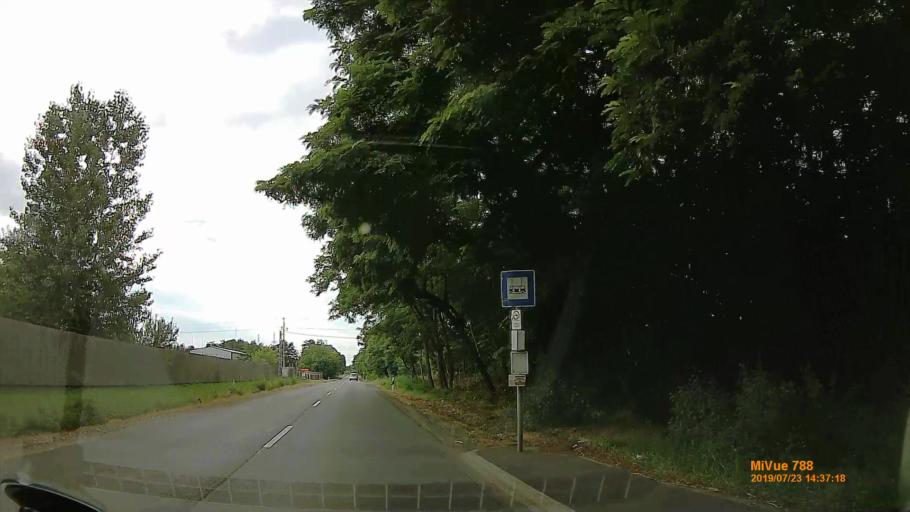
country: HU
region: Szabolcs-Szatmar-Bereg
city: Nyiregyhaza
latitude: 47.9316
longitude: 21.6843
